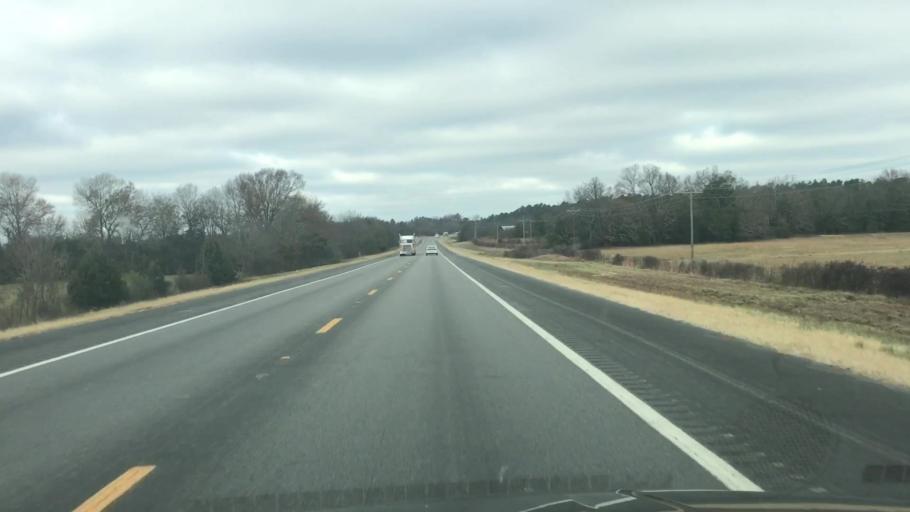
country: US
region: Arkansas
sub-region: Scott County
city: Waldron
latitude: 34.8786
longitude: -94.0977
